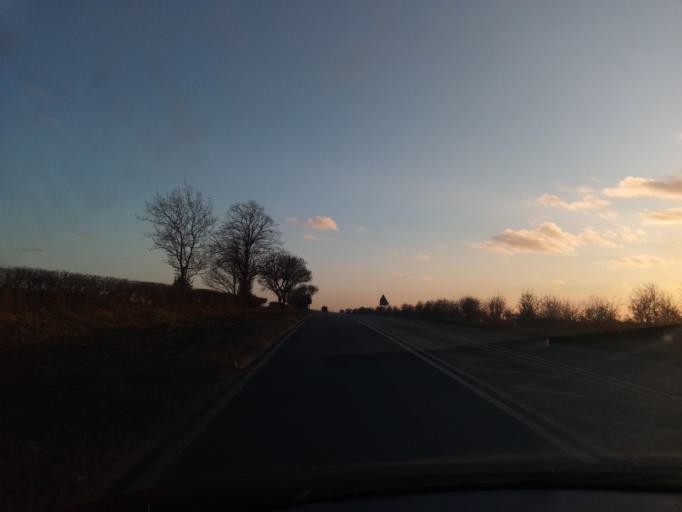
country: GB
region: England
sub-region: Nottinghamshire
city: Farnsfield
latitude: 53.1161
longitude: -1.0647
